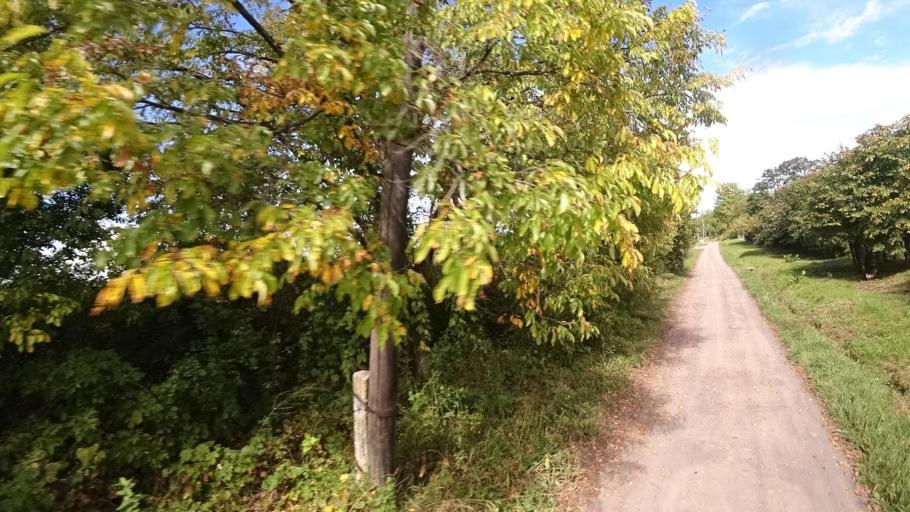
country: RU
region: Primorskiy
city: Yakovlevka
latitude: 44.4357
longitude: 133.5651
